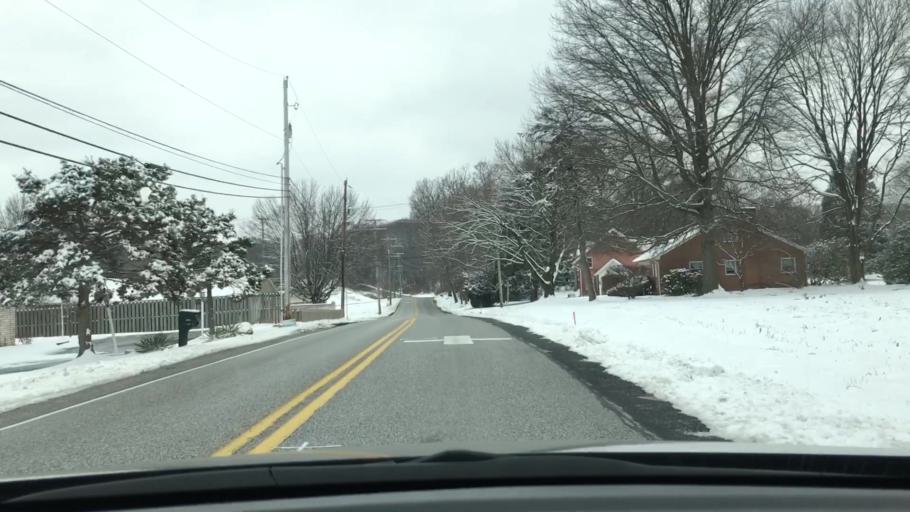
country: US
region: Pennsylvania
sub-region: York County
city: Grantley
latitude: 39.9221
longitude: -76.7176
